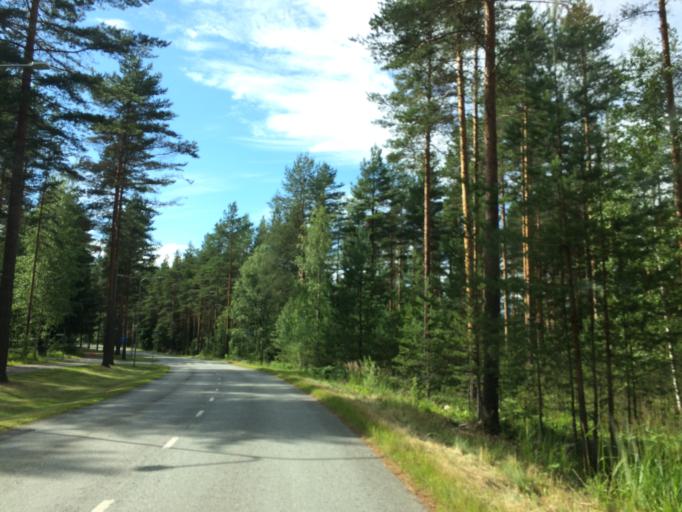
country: FI
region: Haeme
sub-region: Haemeenlinna
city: Turenki
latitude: 60.9395
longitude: 24.6462
